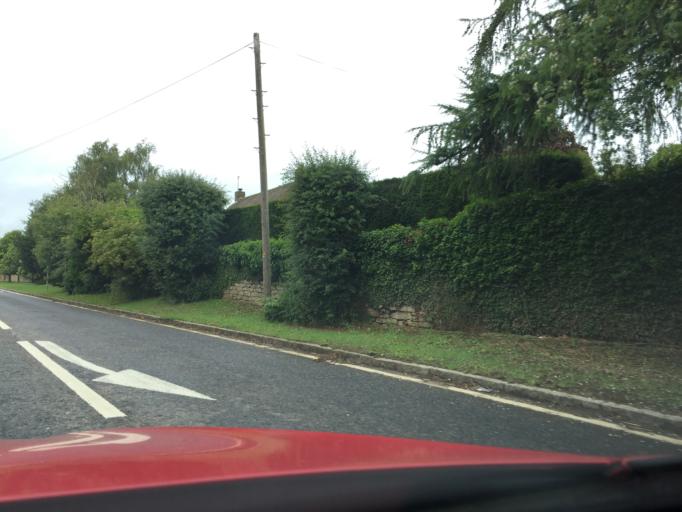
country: GB
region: England
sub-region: Northamptonshire
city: Daventry
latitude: 52.2447
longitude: -1.2090
